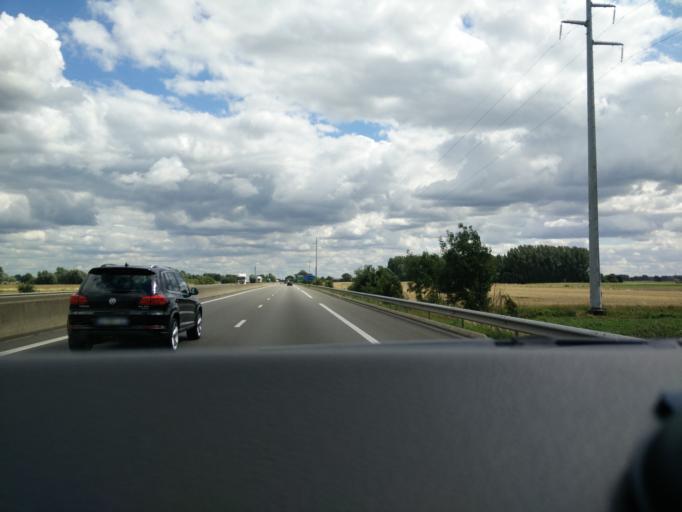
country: FR
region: Nord-Pas-de-Calais
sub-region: Departement du Nord
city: Herzeele
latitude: 50.8776
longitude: 2.5227
